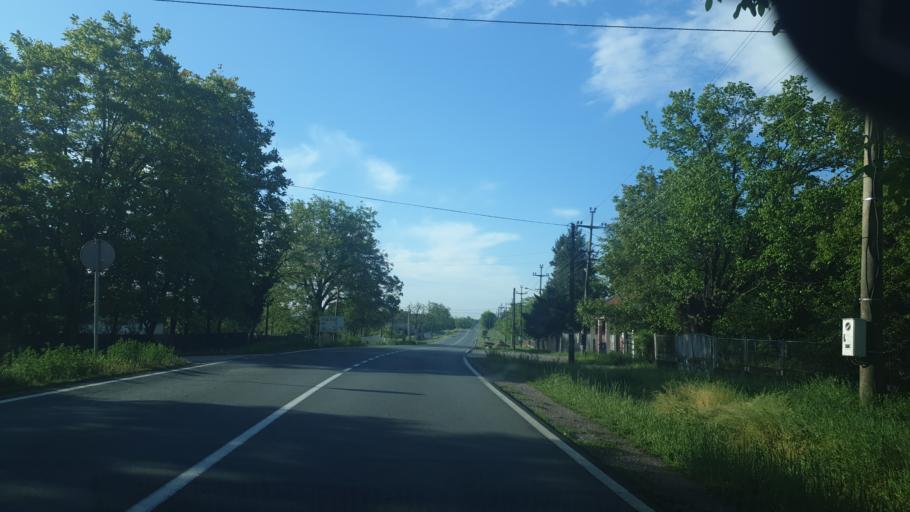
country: RS
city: Stubline
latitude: 44.5911
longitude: 20.1480
